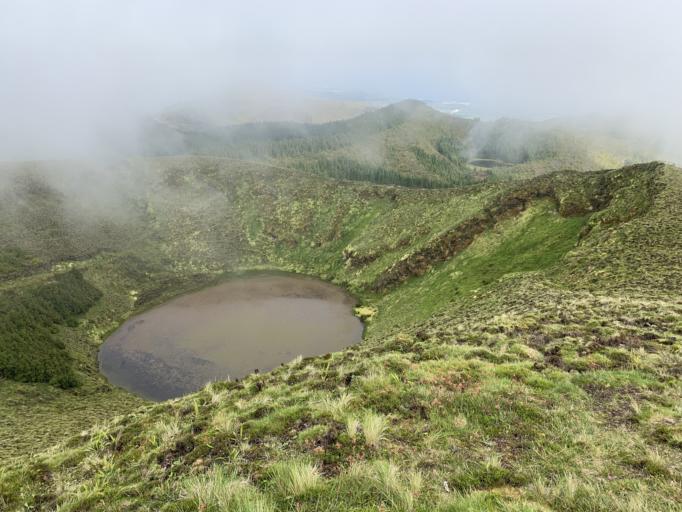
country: PT
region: Azores
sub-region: Ponta Delgada
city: Arrifes
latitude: 37.8272
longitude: -25.7544
